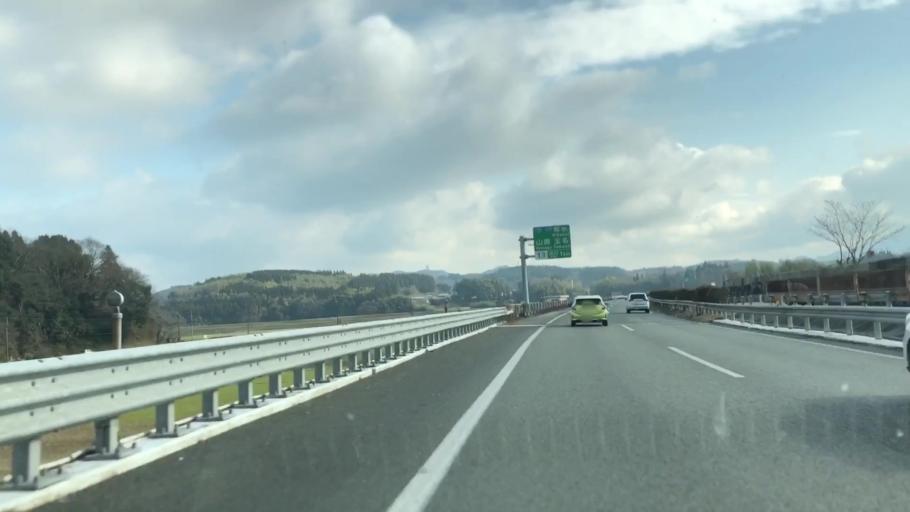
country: JP
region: Kumamoto
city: Tamana
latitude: 32.9957
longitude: 130.5979
